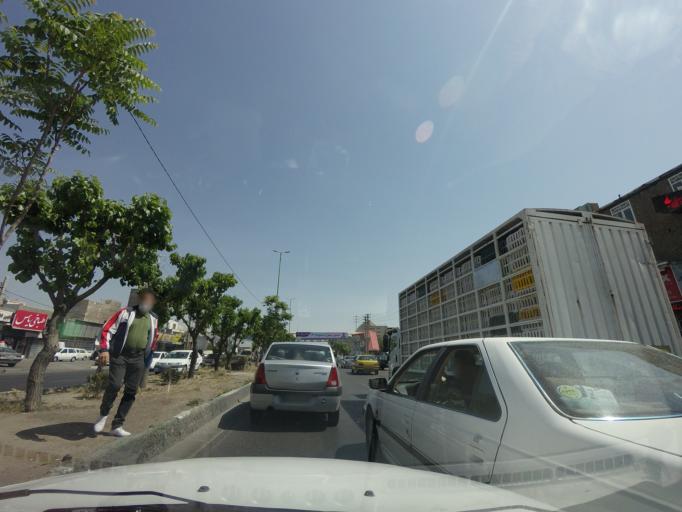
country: IR
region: Tehran
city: Eslamshahr
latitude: 35.6075
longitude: 51.3069
